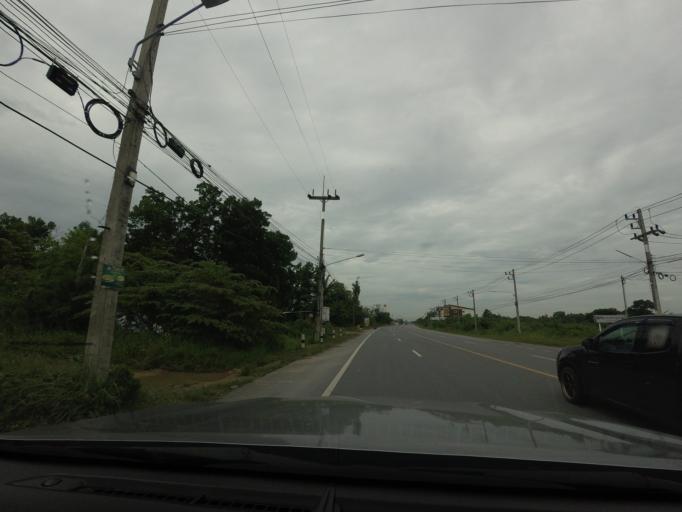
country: TH
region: Nakhon Si Thammarat
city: Nakhon Si Thammarat
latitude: 8.4306
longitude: 99.9852
